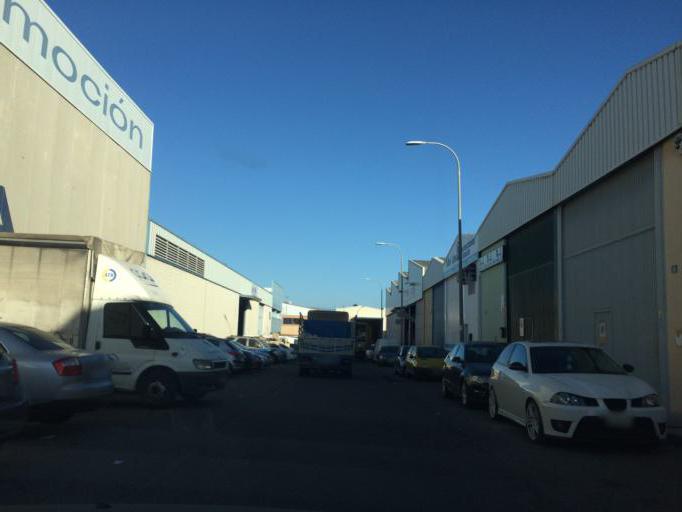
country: ES
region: Andalusia
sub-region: Provincia de Almeria
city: Viator
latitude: 36.8795
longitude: -2.4211
